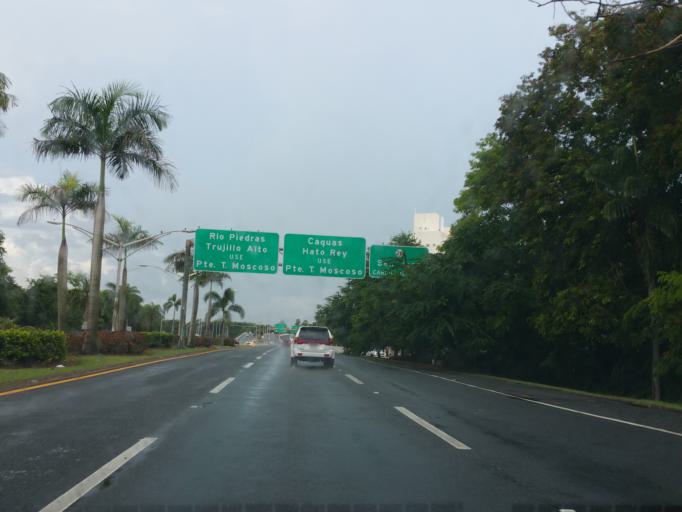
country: PR
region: Carolina
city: Carolina
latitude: 18.4407
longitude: -66.0167
